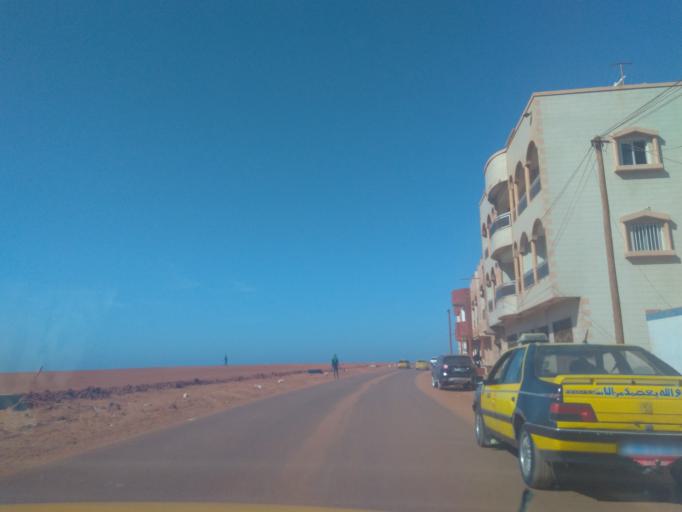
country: SN
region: Dakar
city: Grand Dakar
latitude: 14.7633
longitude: -17.4495
